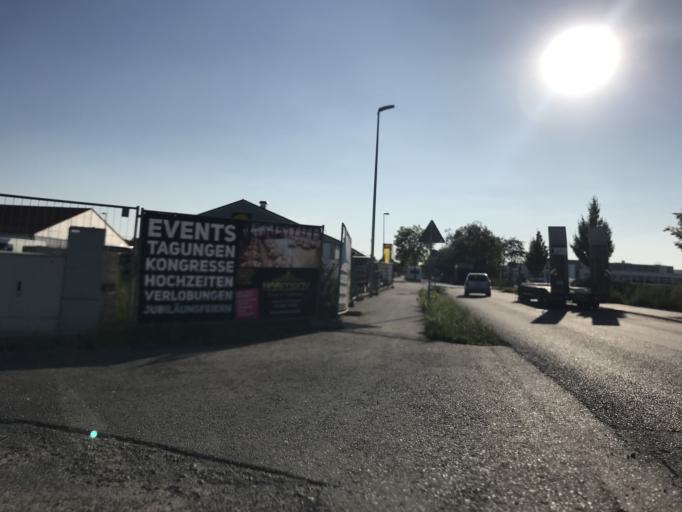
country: DE
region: Rheinland-Pfalz
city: Bodenheim
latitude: 49.9273
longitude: 8.3275
